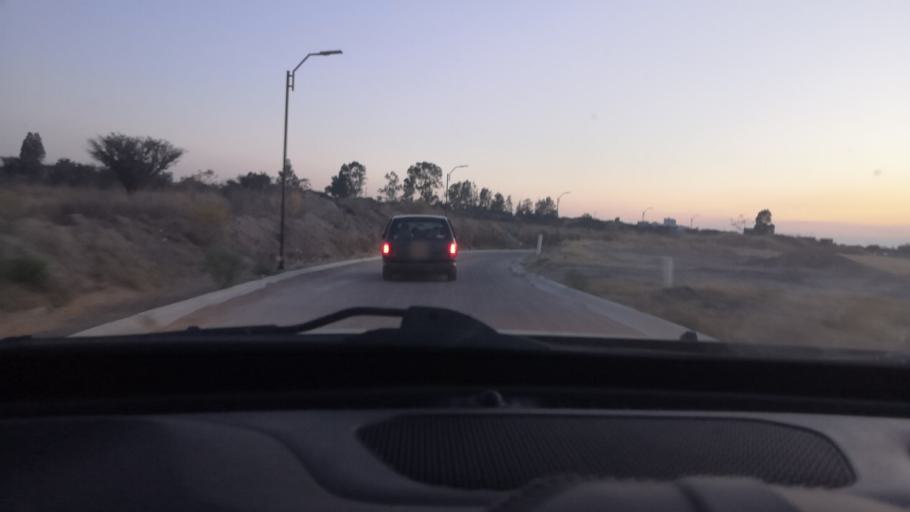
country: MX
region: Guanajuato
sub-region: Leon
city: Fraccionamiento Paseo de las Torres
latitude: 21.2277
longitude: -101.8058
